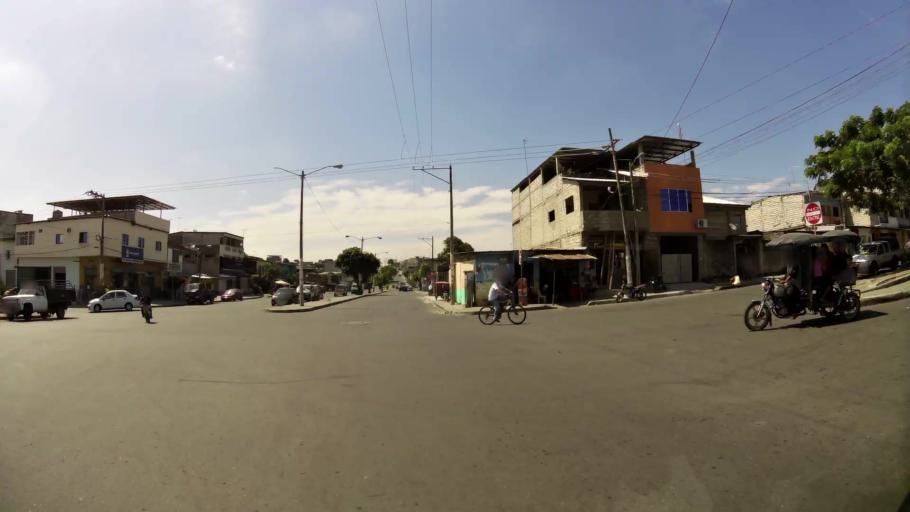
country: EC
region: Guayas
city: Guayaquil
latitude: -2.1260
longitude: -79.9229
